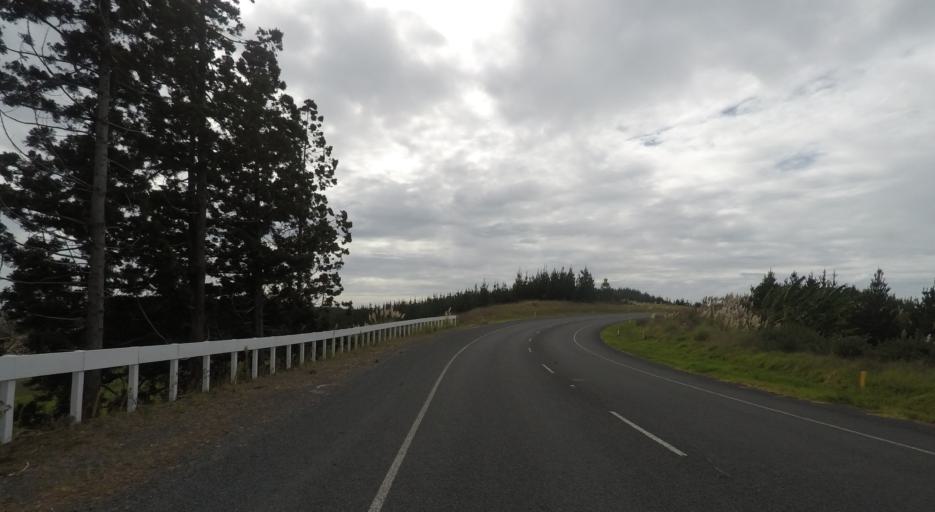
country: NZ
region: Auckland
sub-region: Auckland
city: Rothesay Bay
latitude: -36.6538
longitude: 174.6929
